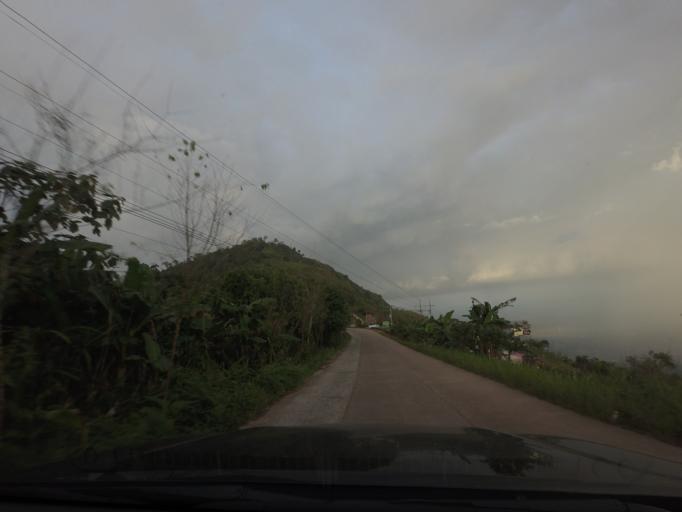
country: TH
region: Phetchabun
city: Lom Kao
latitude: 16.8939
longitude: 101.1038
